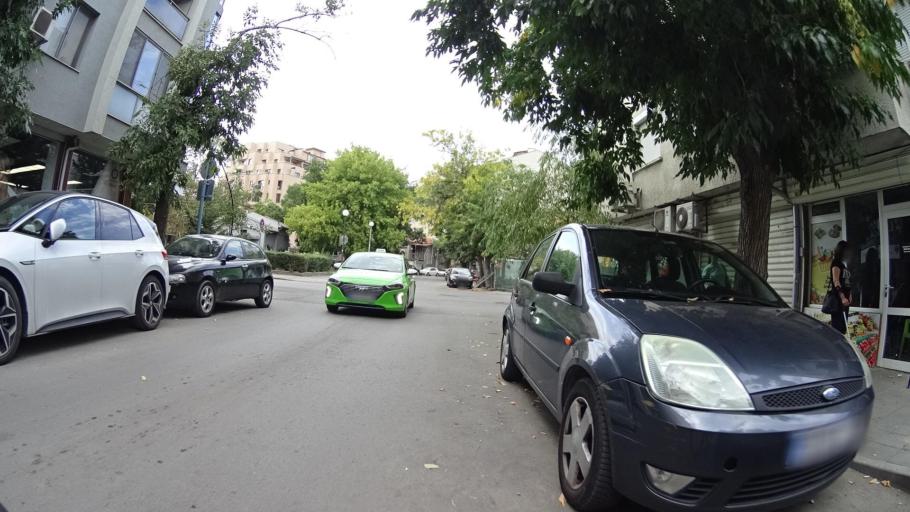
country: BG
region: Plovdiv
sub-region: Obshtina Plovdiv
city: Plovdiv
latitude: 42.1563
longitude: 24.7400
